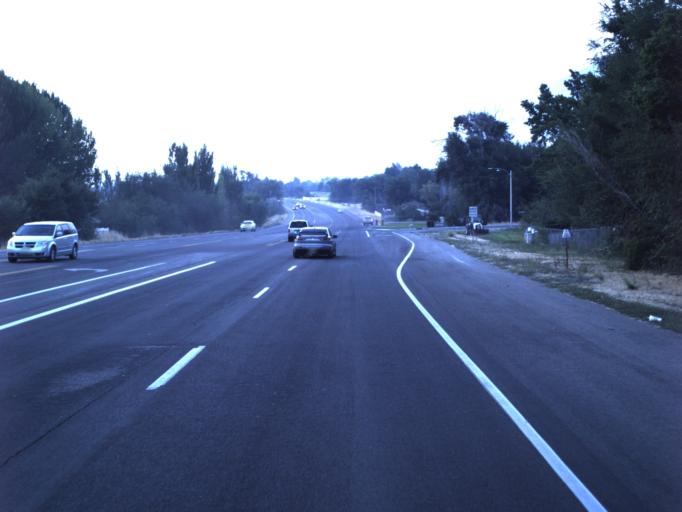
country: US
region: Utah
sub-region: Utah County
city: Springville
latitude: 40.1455
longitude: -111.6030
